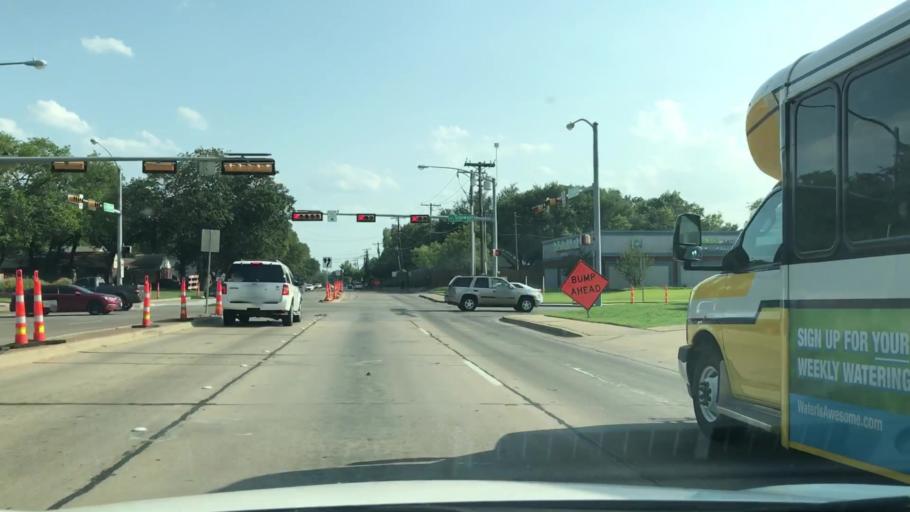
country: US
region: Texas
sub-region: Dallas County
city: Irving
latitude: 32.8299
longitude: -96.9512
